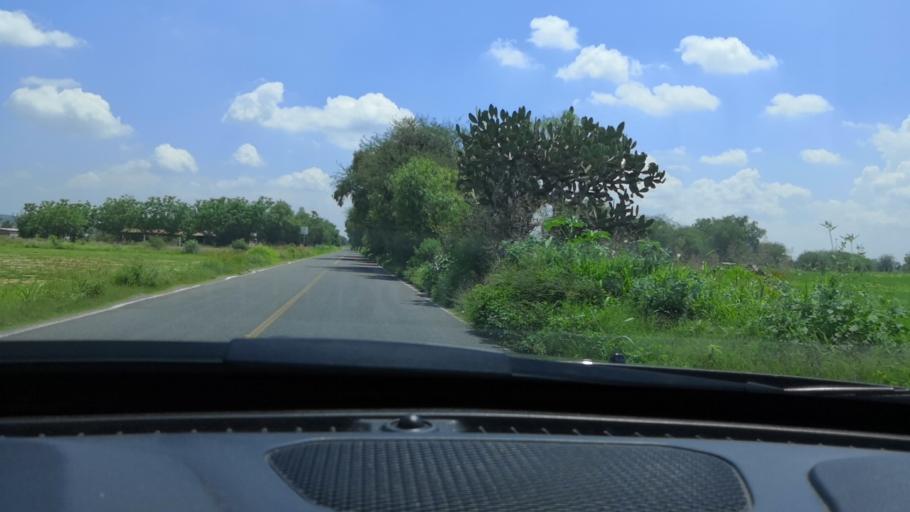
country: MX
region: Guanajuato
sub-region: Silao de la Victoria
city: El Refugio de los Sauces
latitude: 20.9622
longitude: -101.5866
